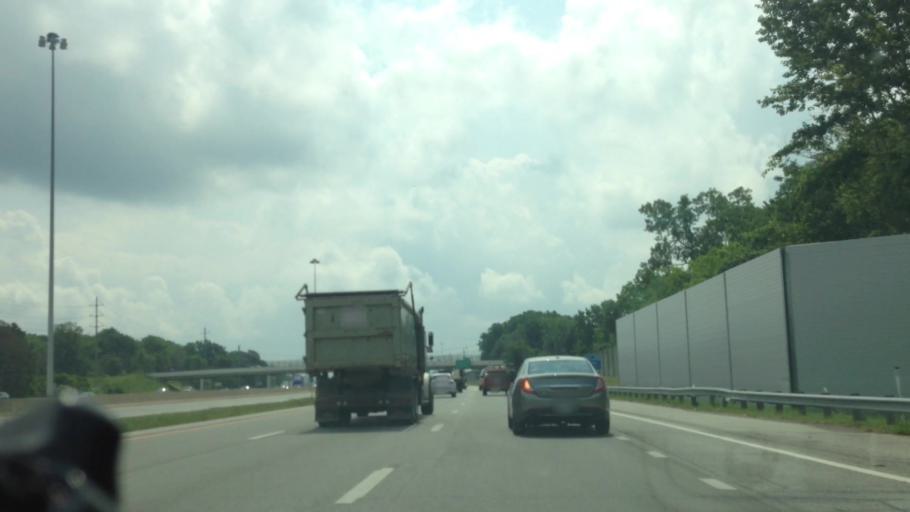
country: US
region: Ohio
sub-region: Cuyahoga County
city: Mayfield Heights
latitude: 41.5330
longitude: -81.4487
